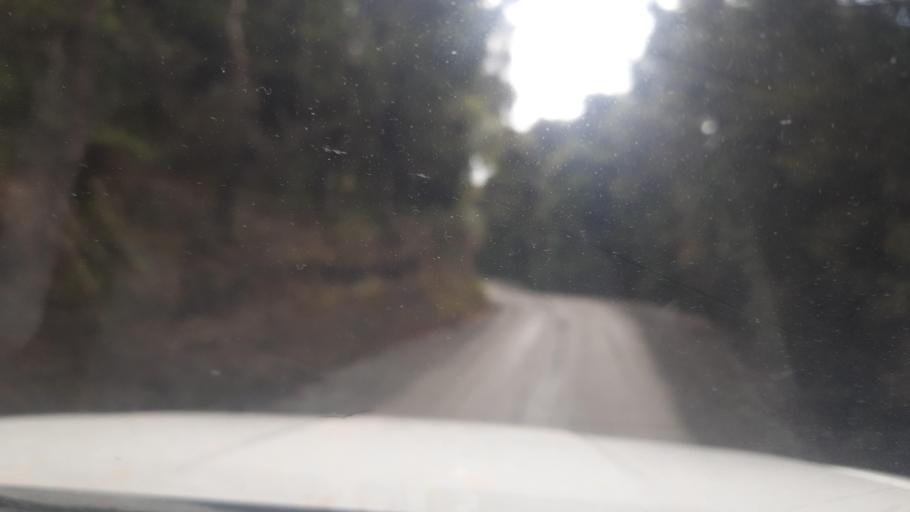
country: NZ
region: Northland
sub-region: Far North District
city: Taipa
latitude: -35.0679
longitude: 173.5262
